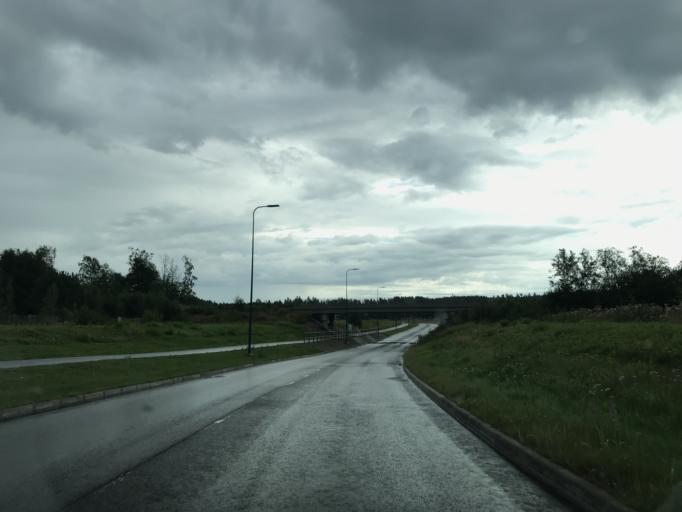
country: FI
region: Uusimaa
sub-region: Helsinki
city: Vihti
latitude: 60.3240
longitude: 24.3059
